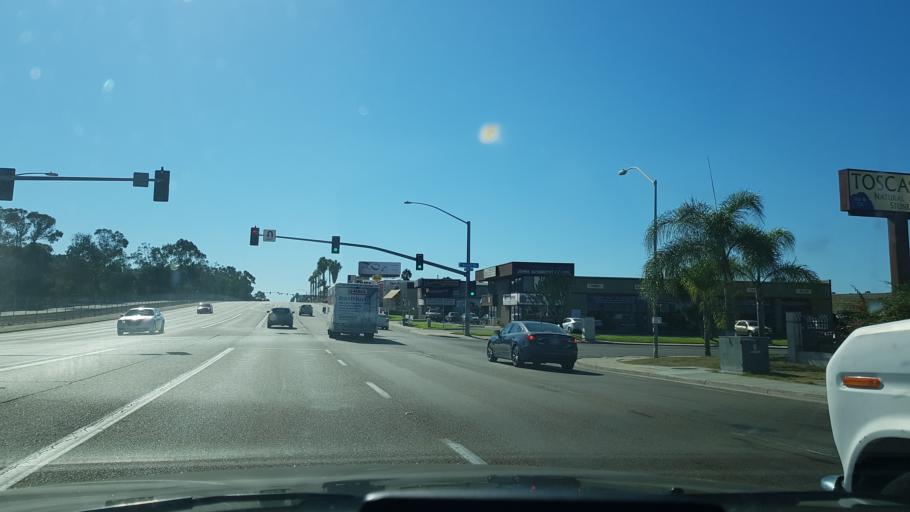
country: US
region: California
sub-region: San Diego County
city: Fairbanks Ranch
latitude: 32.8886
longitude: -117.1449
